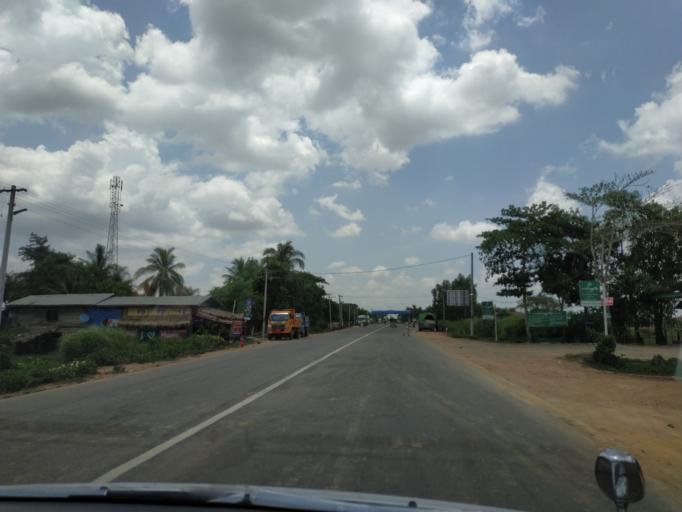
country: MM
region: Bago
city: Bago
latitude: 17.4719
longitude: 96.5439
